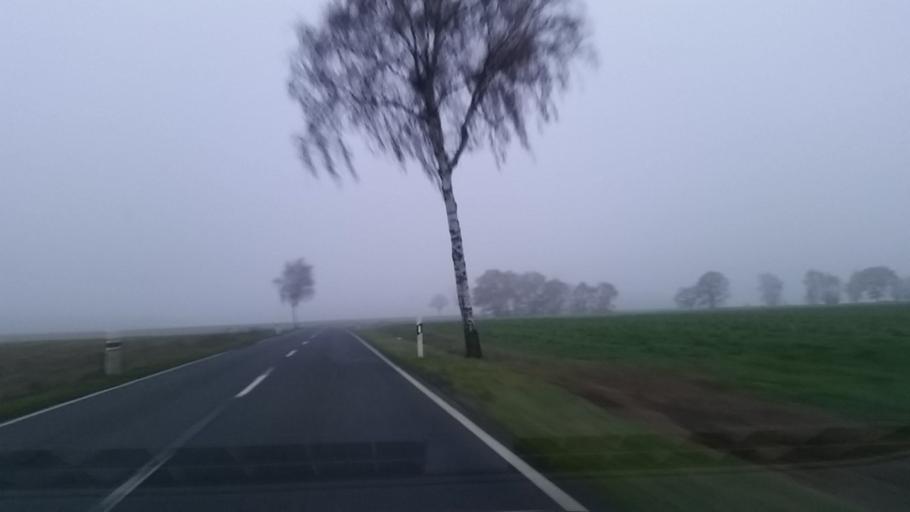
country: DE
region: Lower Saxony
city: Wittingen
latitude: 52.6851
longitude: 10.8067
